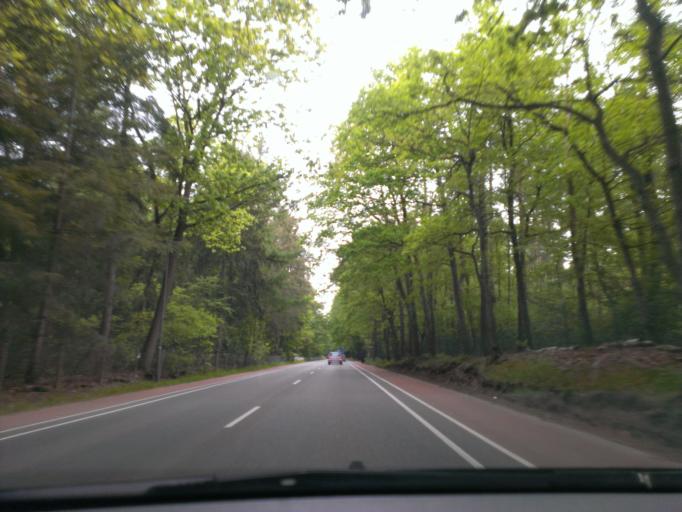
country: NL
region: Gelderland
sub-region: Gemeente Heerde
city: Heerde
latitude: 52.4211
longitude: 6.0607
